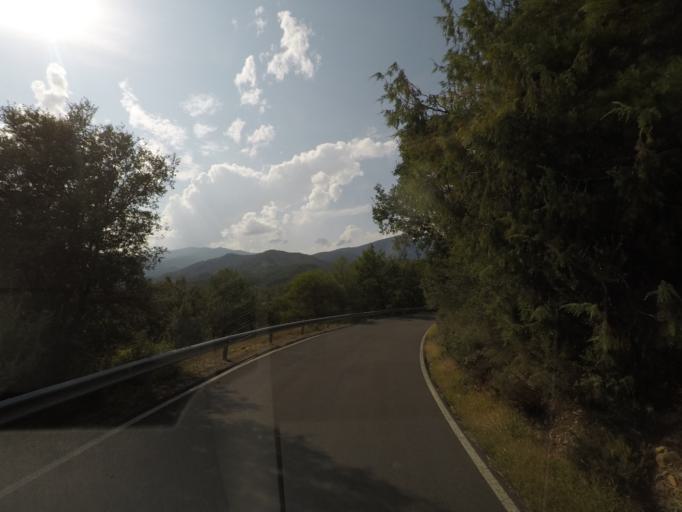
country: ES
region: Aragon
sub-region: Provincia de Huesca
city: Laspuna
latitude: 42.5042
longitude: 0.1332
